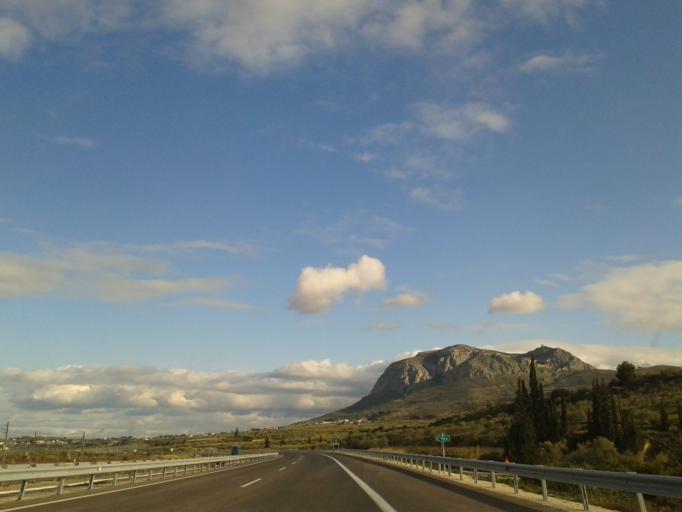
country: GR
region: Peloponnese
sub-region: Nomos Korinthias
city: Lekhaio
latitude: 37.9102
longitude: 22.8399
